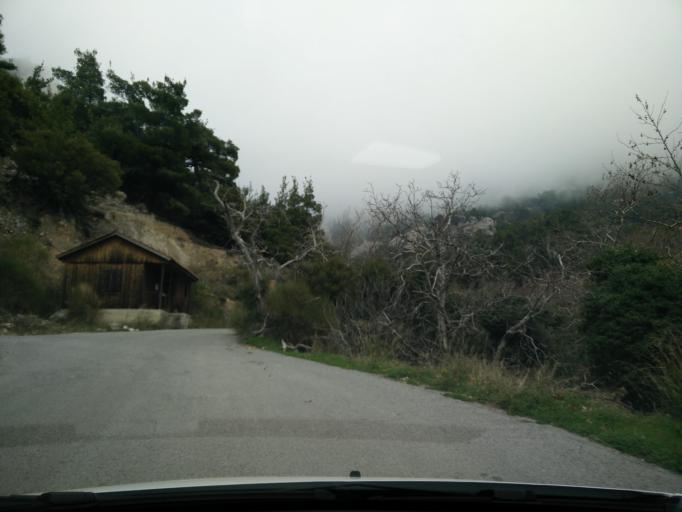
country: GR
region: Crete
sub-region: Nomos Lasithiou
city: Kritsa
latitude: 35.0491
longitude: 25.4894
